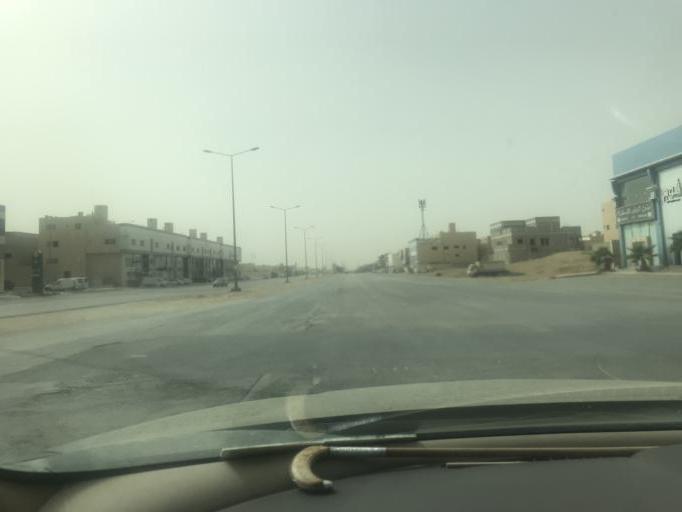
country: SA
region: Ar Riyad
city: Riyadh
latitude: 24.8067
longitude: 46.6023
